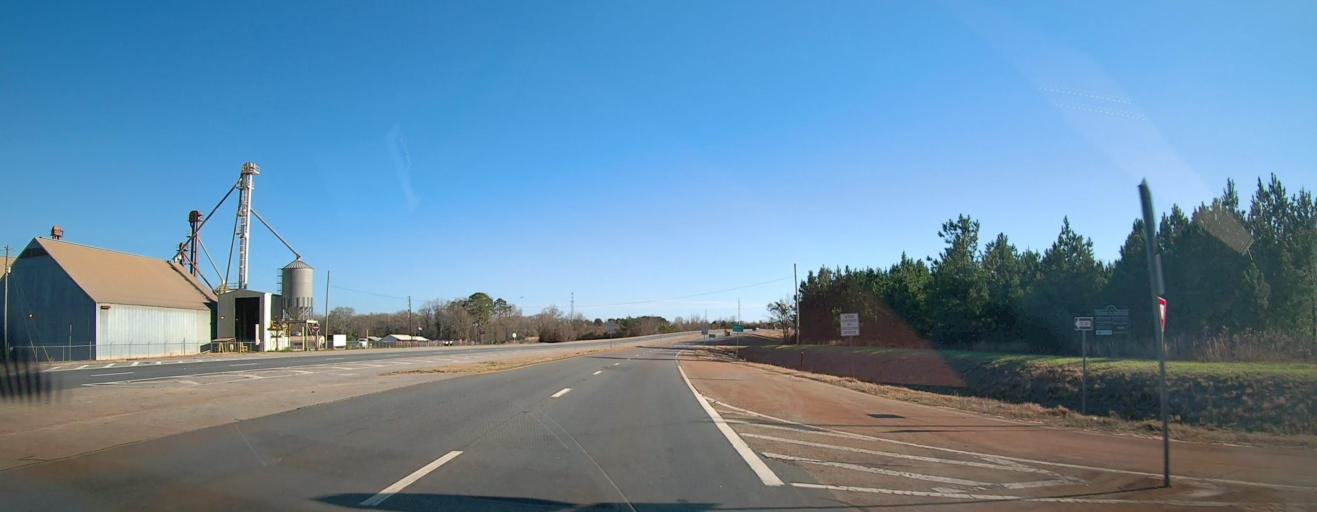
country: US
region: Georgia
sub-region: Sumter County
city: Americus
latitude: 31.9160
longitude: -84.2607
